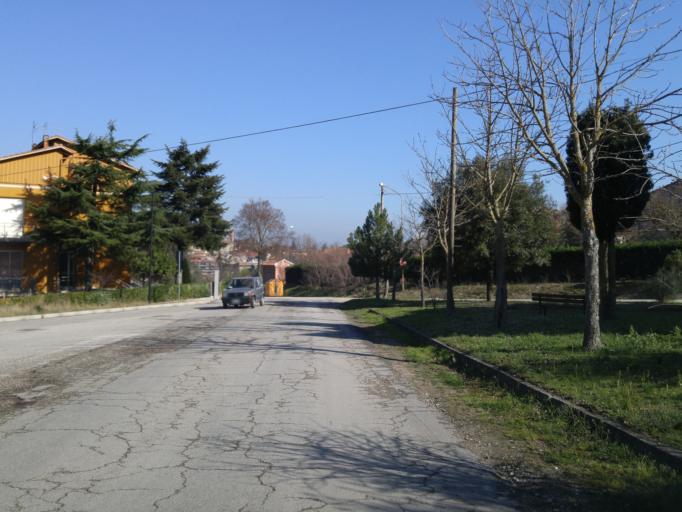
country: IT
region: The Marches
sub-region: Provincia di Pesaro e Urbino
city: Fossombrone
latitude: 43.6833
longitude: 12.8033
